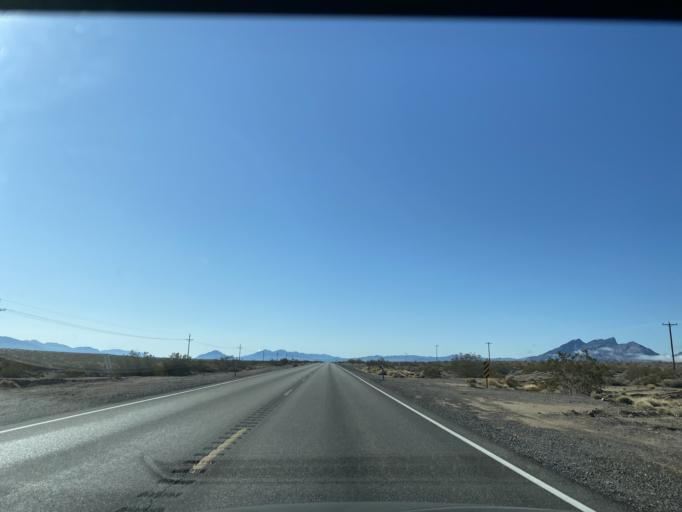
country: US
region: Nevada
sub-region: Nye County
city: Pahrump
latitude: 36.4717
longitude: -116.4216
